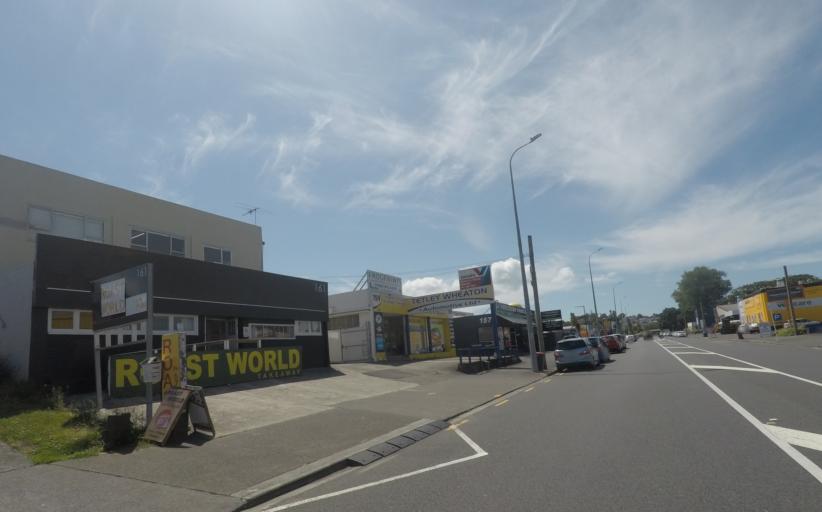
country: NZ
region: Auckland
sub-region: Auckland
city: Tamaki
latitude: -36.8756
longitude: 174.8541
